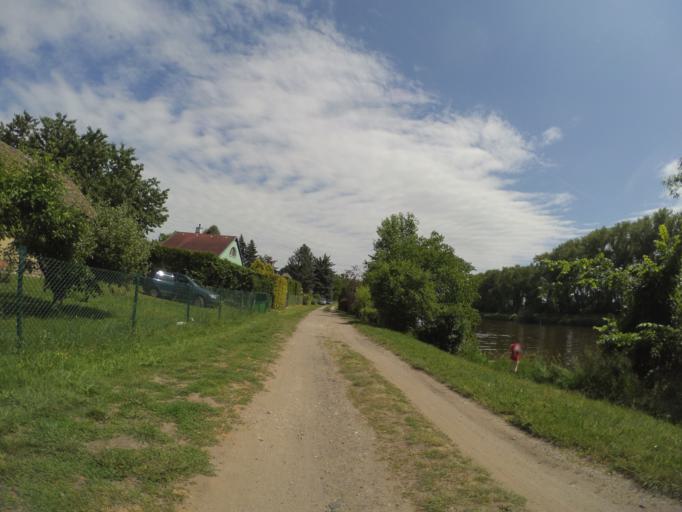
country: CZ
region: Central Bohemia
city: Milovice
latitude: 50.1725
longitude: 14.9005
